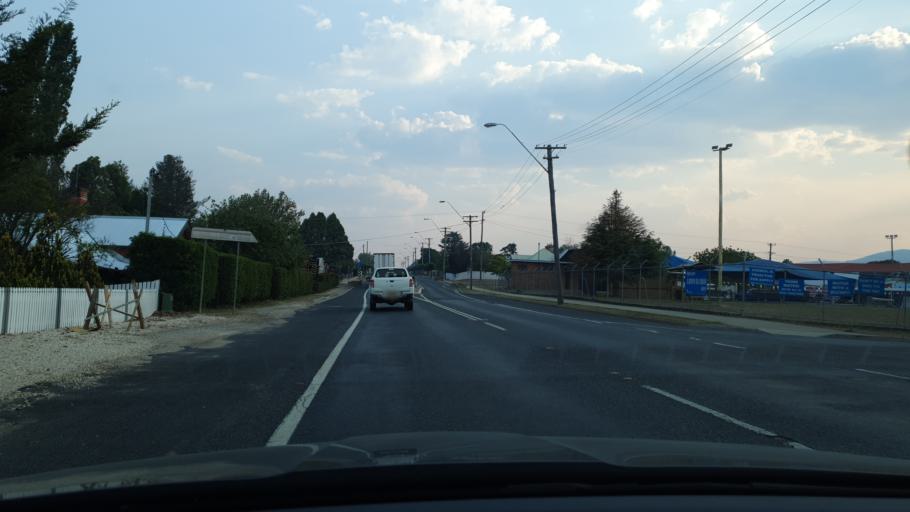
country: AU
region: New South Wales
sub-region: Tenterfield Municipality
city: Carrolls Creek
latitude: -29.0465
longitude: 152.0205
